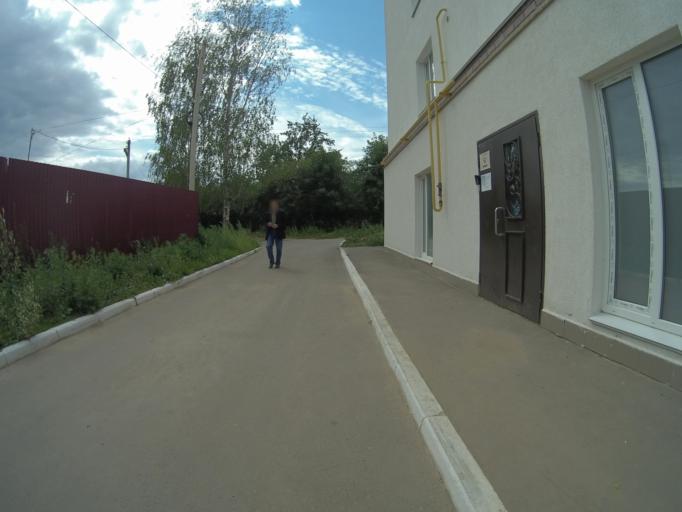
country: RU
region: Vladimir
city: Bogolyubovo
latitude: 56.1979
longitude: 40.5317
